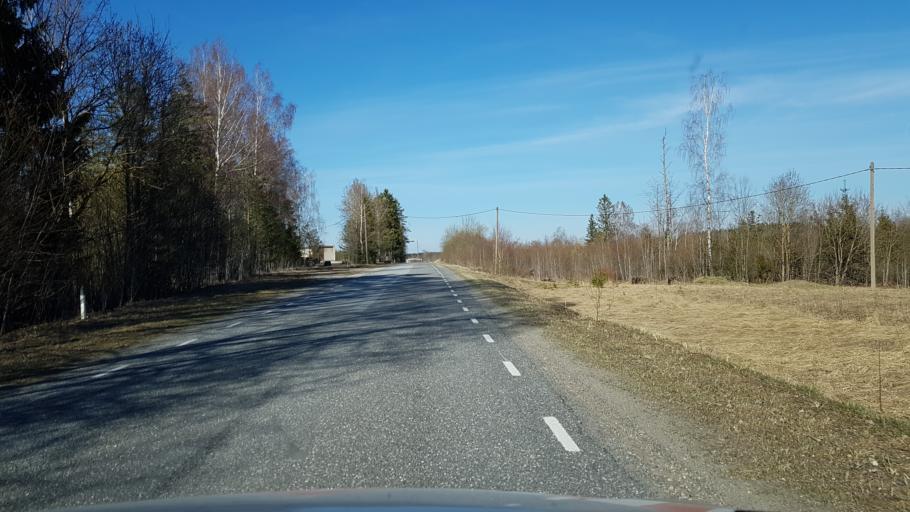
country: EE
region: Laeaene-Virumaa
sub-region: Rakke vald
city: Rakke
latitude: 58.9897
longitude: 26.2683
